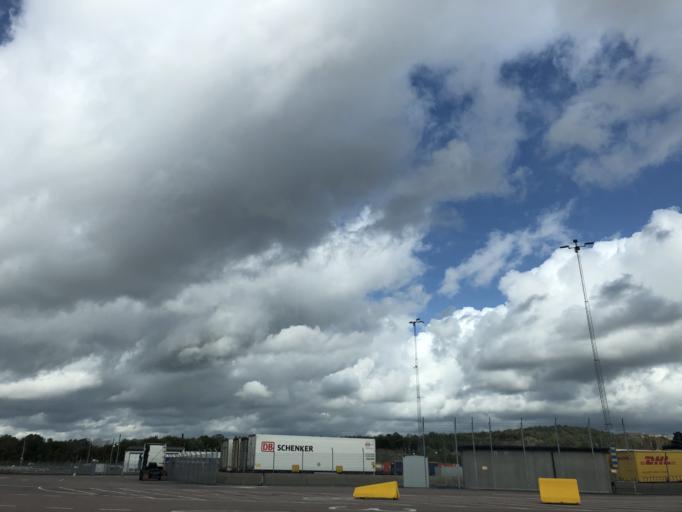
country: SE
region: Vaestra Goetaland
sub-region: Goteborg
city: Torslanda
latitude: 57.6949
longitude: 11.8302
